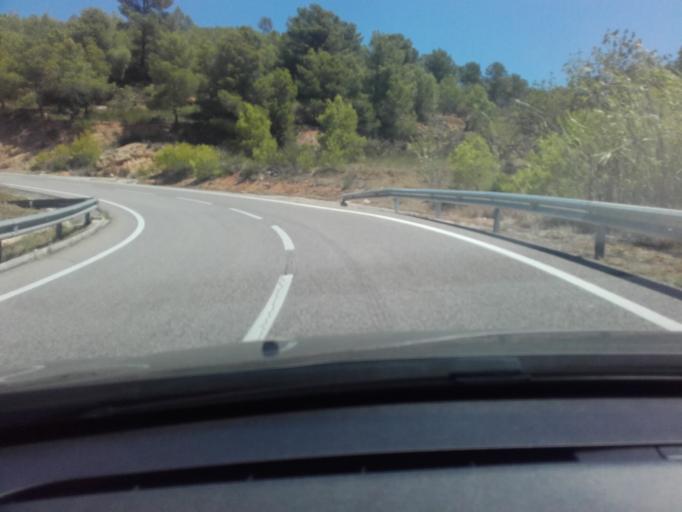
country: ES
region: Catalonia
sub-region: Provincia de Tarragona
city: la Bisbal del Penedes
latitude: 41.2891
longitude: 1.4889
